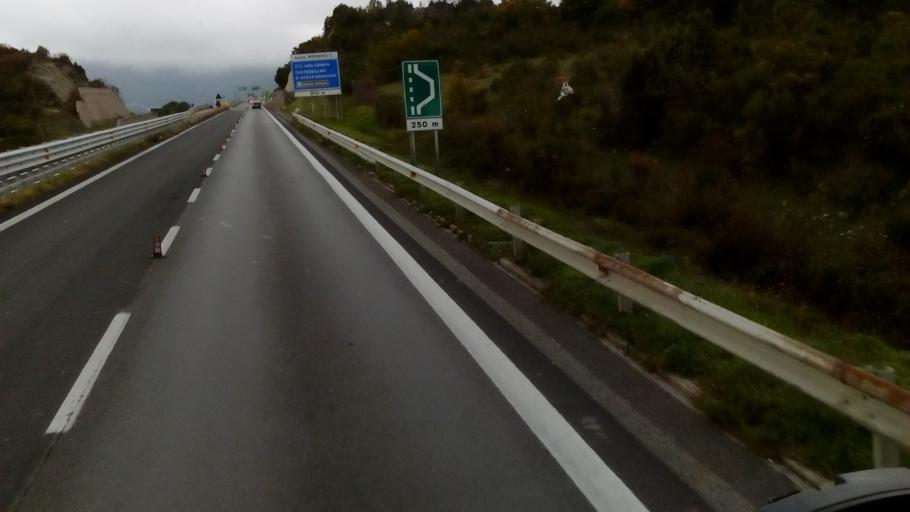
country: IT
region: Calabria
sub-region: Provincia di Cosenza
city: Morano Calabro
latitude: 39.8702
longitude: 16.1753
